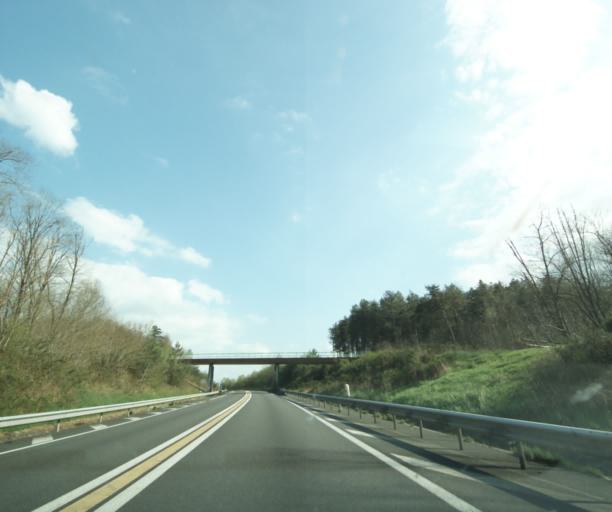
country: FR
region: Auvergne
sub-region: Departement de l'Allier
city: Diou
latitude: 46.4796
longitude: 3.8311
